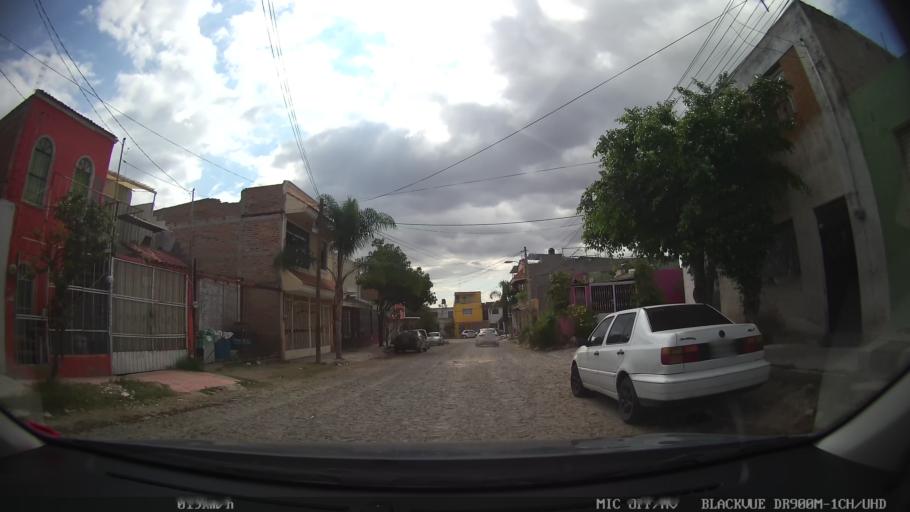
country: MX
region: Jalisco
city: Tlaquepaque
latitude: 20.6757
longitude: -103.2538
